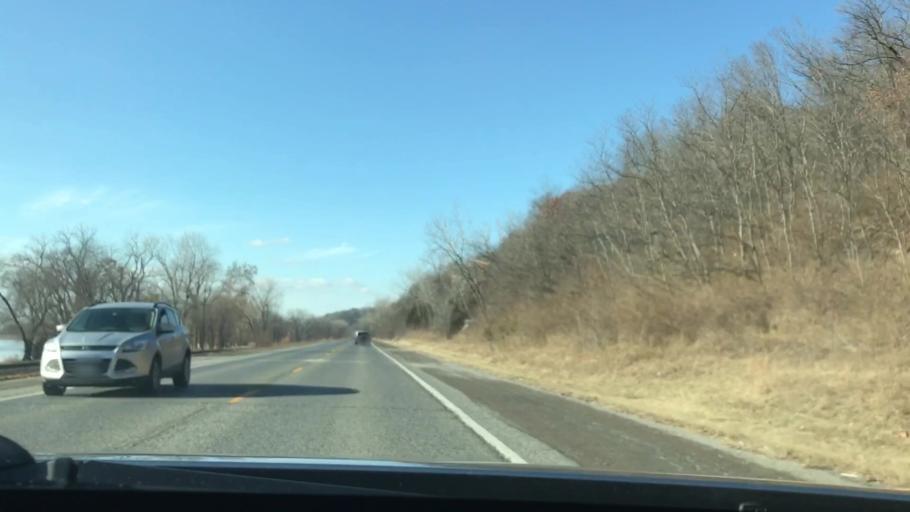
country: US
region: Missouri
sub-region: Platte County
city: Parkville
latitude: 39.1838
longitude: -94.6689
